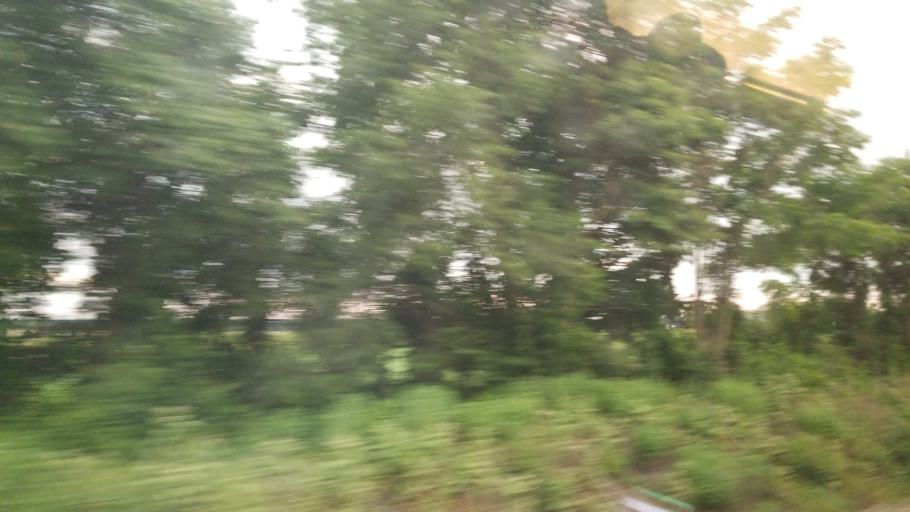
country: US
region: Virginia
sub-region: Culpeper County
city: Culpeper
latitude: 38.4328
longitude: -77.9964
